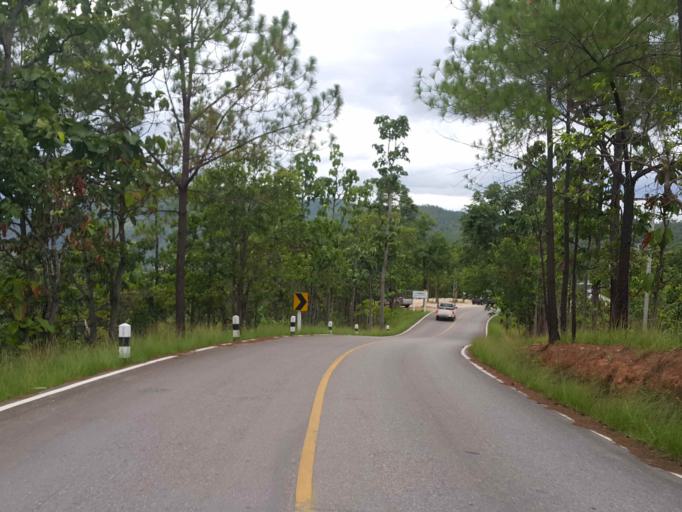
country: TH
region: Chiang Mai
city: Mae Chaem
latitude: 18.5113
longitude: 98.4261
